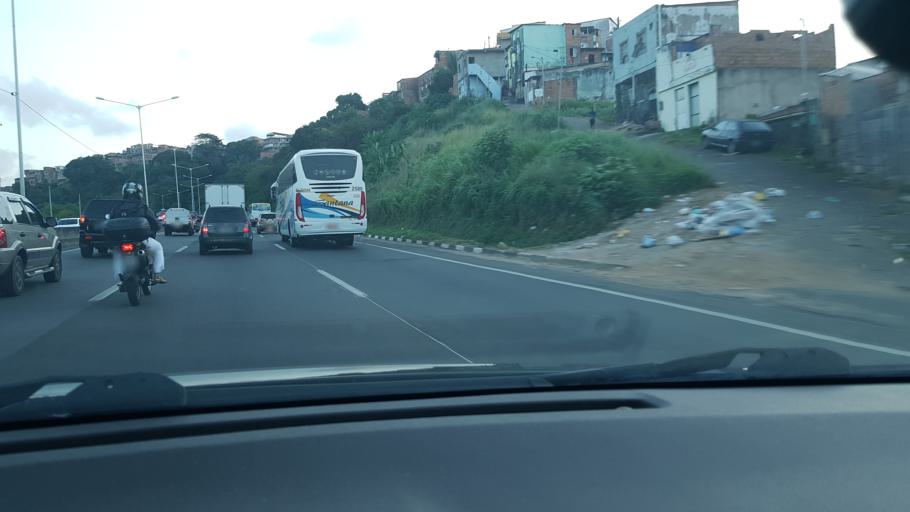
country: BR
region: Bahia
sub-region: Salvador
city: Salvador
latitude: -12.9337
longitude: -38.4718
